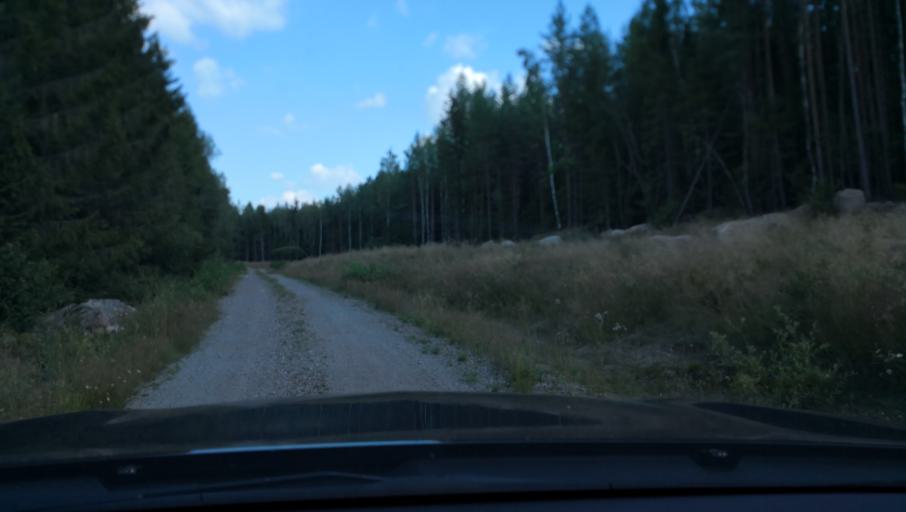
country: SE
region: Vaestmanland
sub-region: Vasteras
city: Skultuna
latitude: 59.7088
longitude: 16.3672
